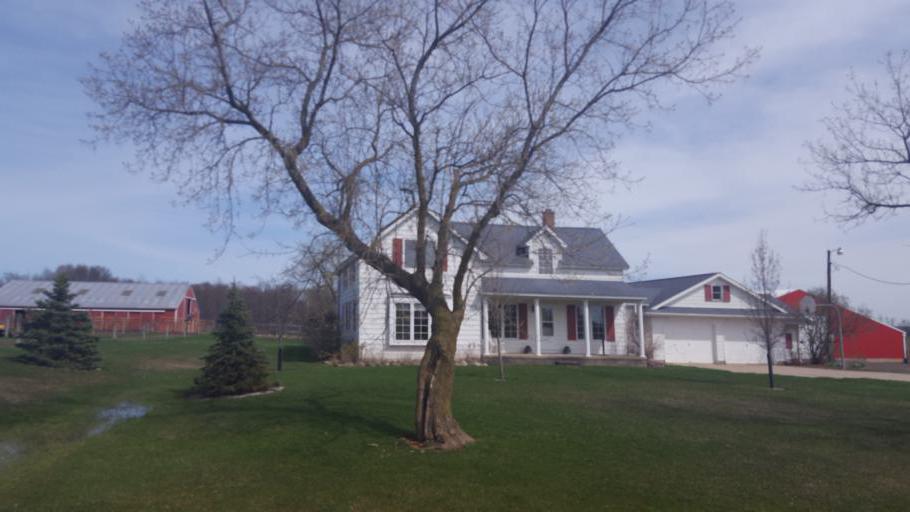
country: US
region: Michigan
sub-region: Gladwin County
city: Gladwin
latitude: 44.0448
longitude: -84.4674
